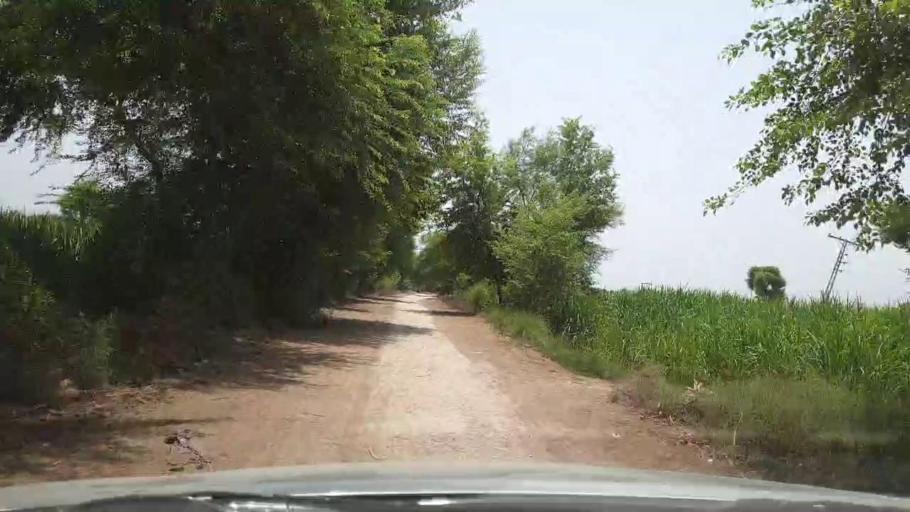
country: PK
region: Sindh
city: Pano Aqil
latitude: 27.8633
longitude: 69.0645
